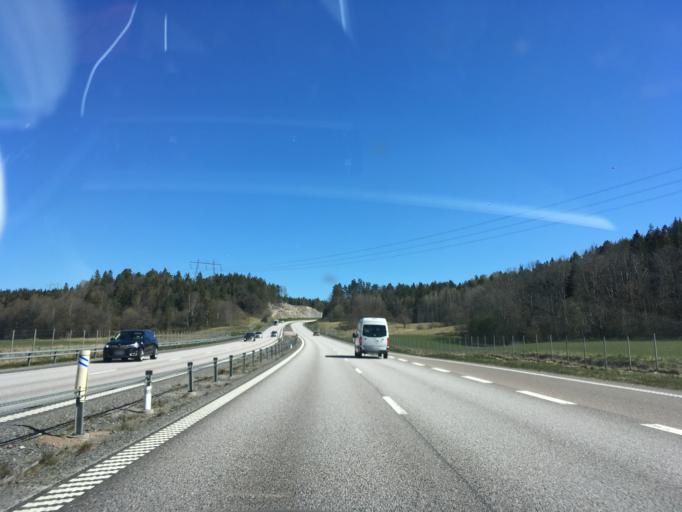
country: SE
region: Vaestra Goetaland
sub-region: Trollhattan
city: Sjuntorp
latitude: 58.2122
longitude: 12.1851
